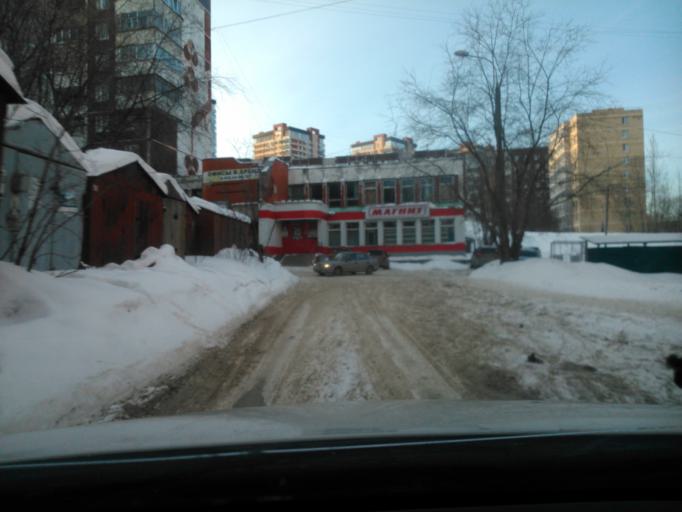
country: RU
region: Perm
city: Perm
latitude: 58.0000
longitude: 56.3087
